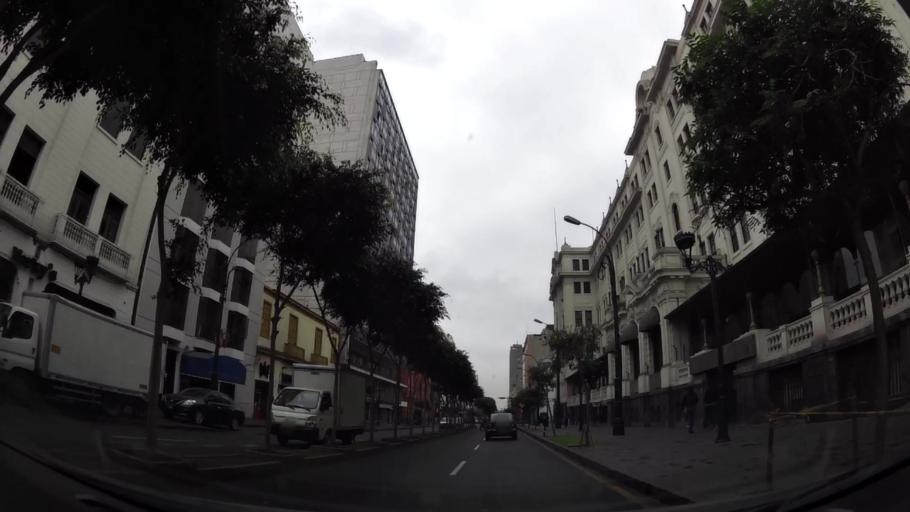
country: PE
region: Lima
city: Lima
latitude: -12.0511
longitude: -77.0354
